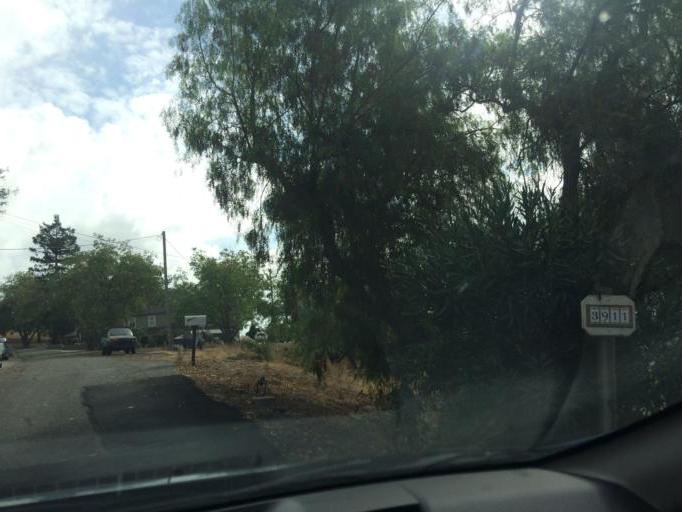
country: US
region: California
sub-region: Santa Clara County
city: East Foothills
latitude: 37.3401
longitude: -121.7692
